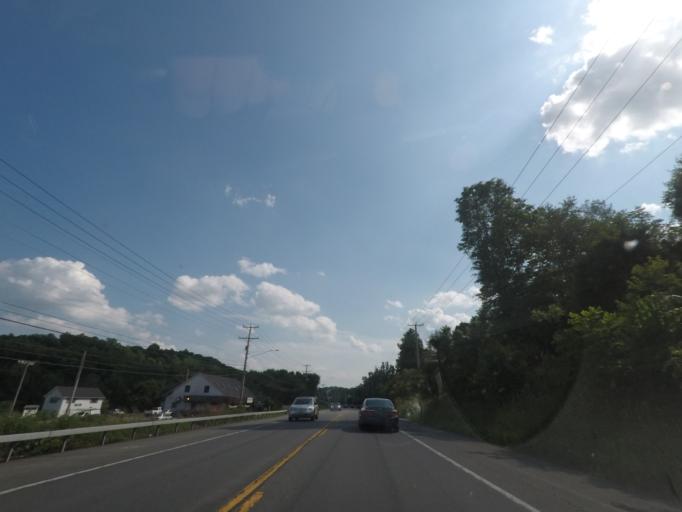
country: US
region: New York
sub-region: Ulster County
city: Marlboro
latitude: 41.5812
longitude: -73.9875
